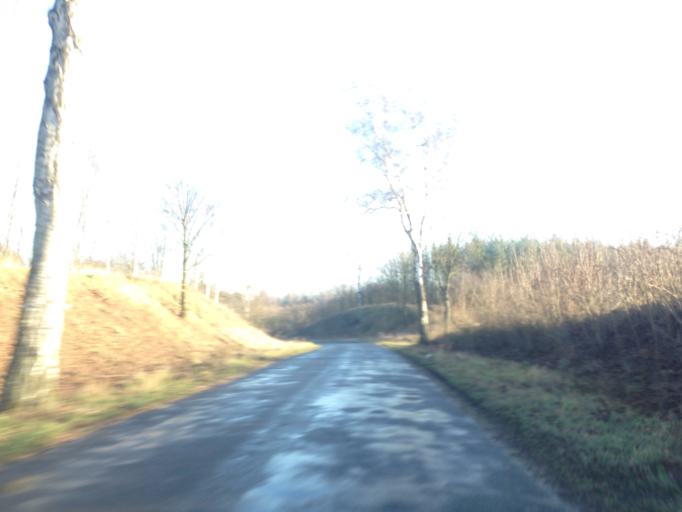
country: PL
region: Kujawsko-Pomorskie
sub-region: Powiat grudziadzki
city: Swiecie nad Osa
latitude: 53.4475
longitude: 19.1312
